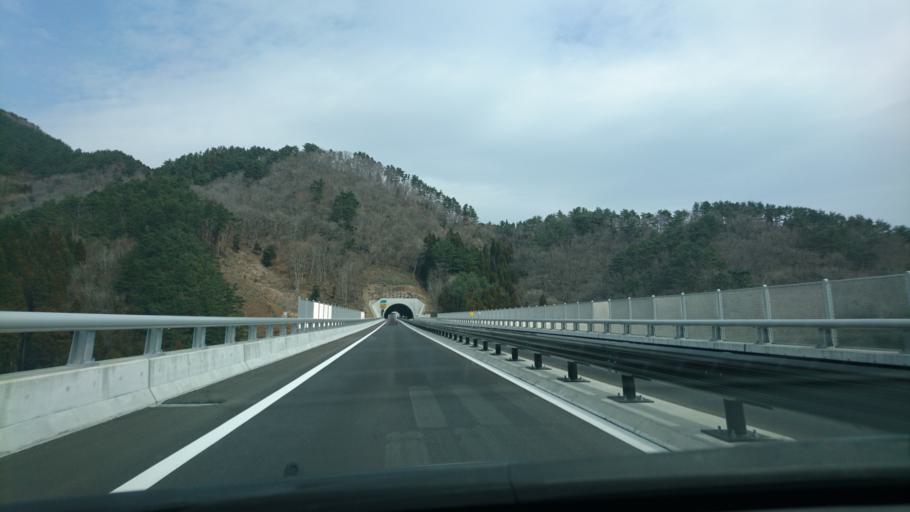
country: JP
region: Iwate
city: Kamaishi
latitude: 39.2047
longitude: 141.8596
